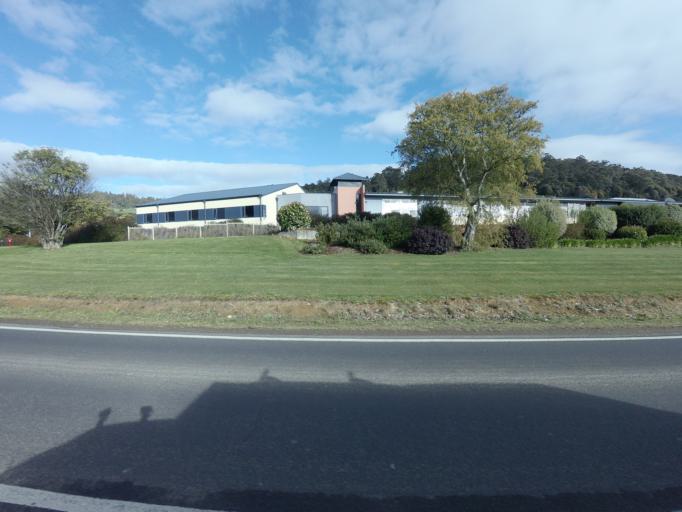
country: AU
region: Tasmania
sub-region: Huon Valley
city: Franklin
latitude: -43.0820
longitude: 147.0166
